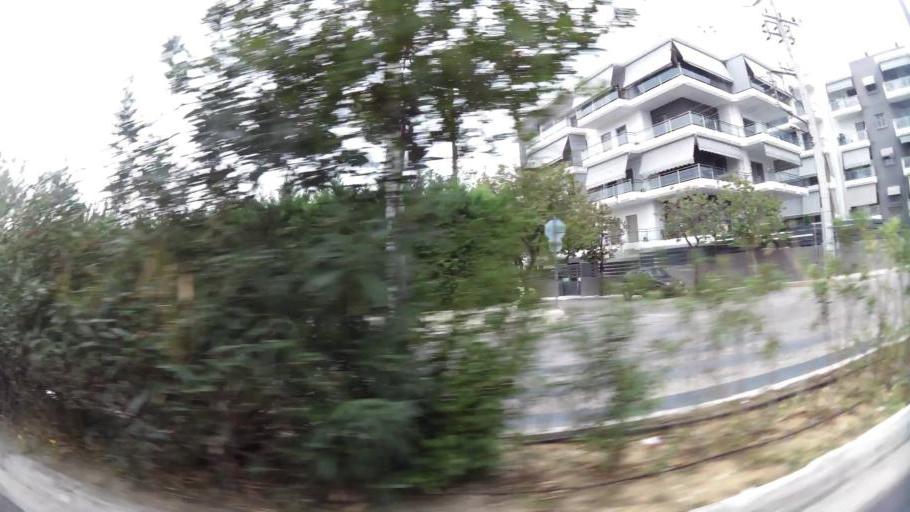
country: GR
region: Attica
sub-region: Nomarchia Athinas
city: Ilion
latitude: 38.0384
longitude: 23.7118
